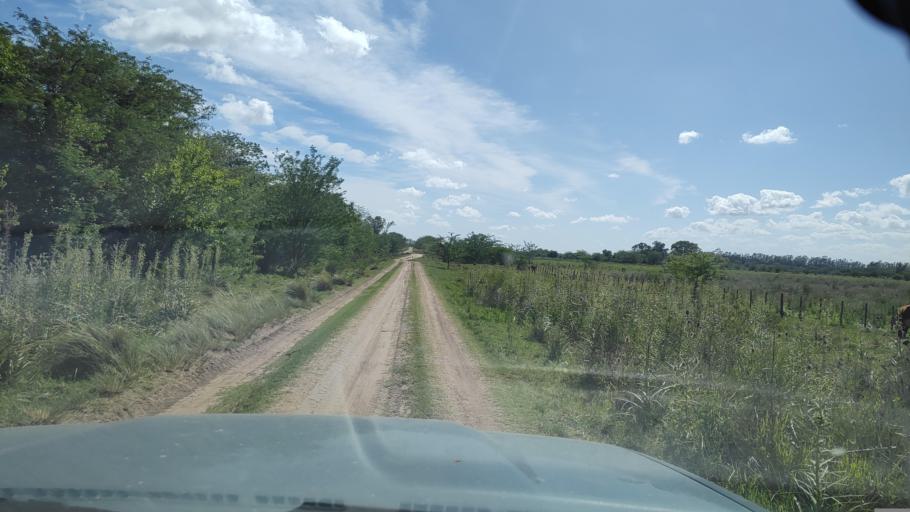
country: AR
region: Buenos Aires
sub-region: Partido de Lujan
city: Lujan
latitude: -34.5221
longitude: -59.1705
